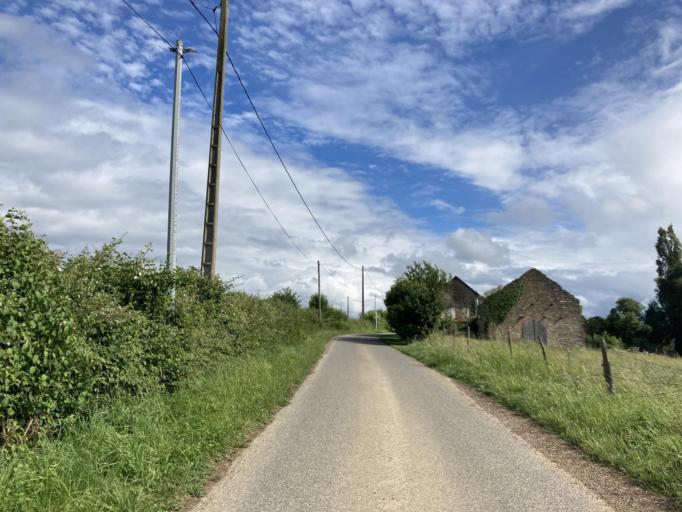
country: FR
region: Aquitaine
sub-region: Departement des Pyrenees-Atlantiques
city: Ledeuix
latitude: 43.2550
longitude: -0.6248
